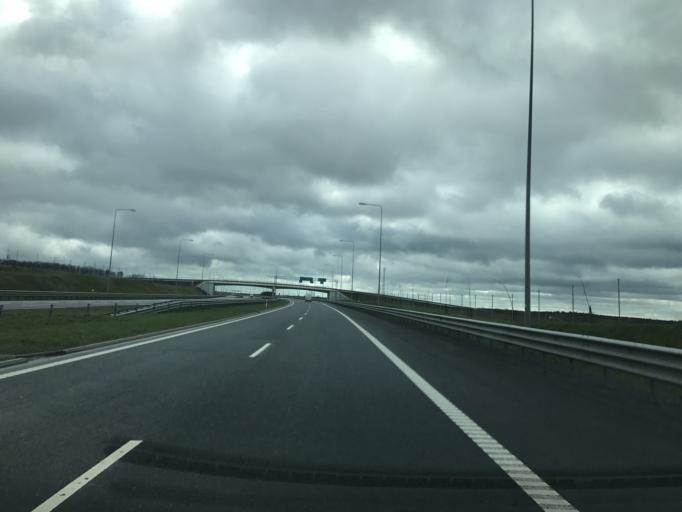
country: PL
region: Warmian-Masurian Voivodeship
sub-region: Powiat olsztynski
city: Olsztynek
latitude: 53.5933
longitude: 20.2604
